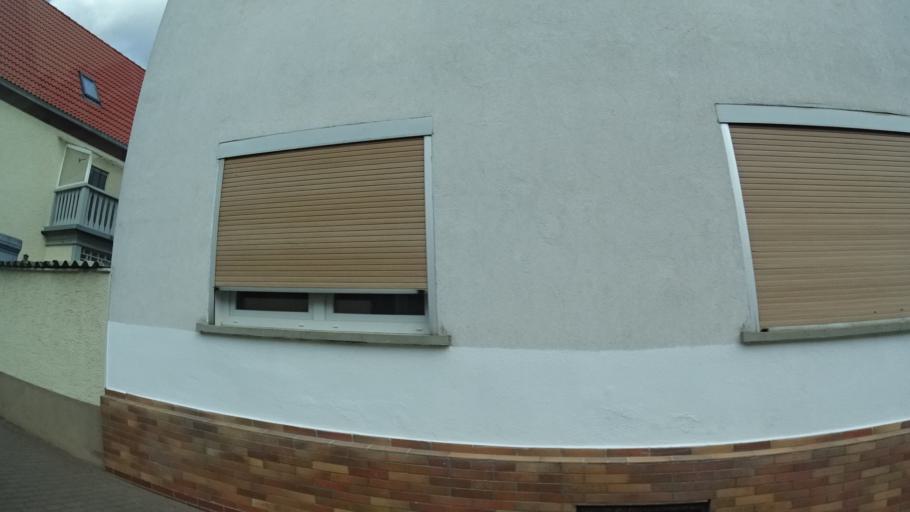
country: DE
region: Bavaria
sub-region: Regierungsbezirk Unterfranken
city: Grafenrheinfeld
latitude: 49.9991
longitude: 10.1980
